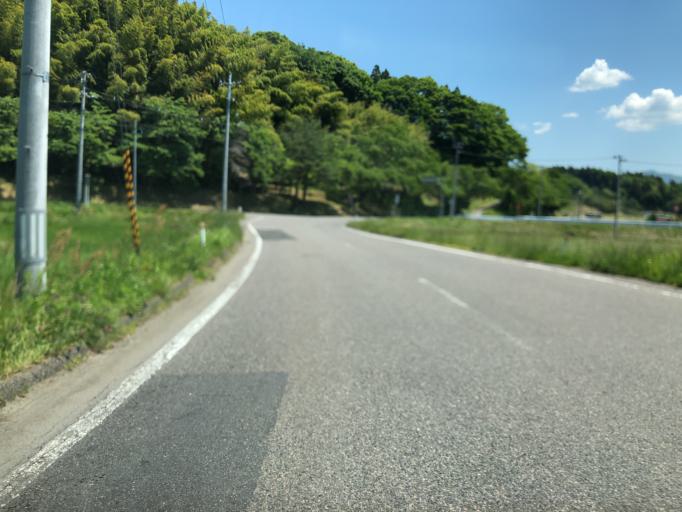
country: JP
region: Fukushima
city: Funehikimachi-funehiki
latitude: 37.4903
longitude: 140.5232
